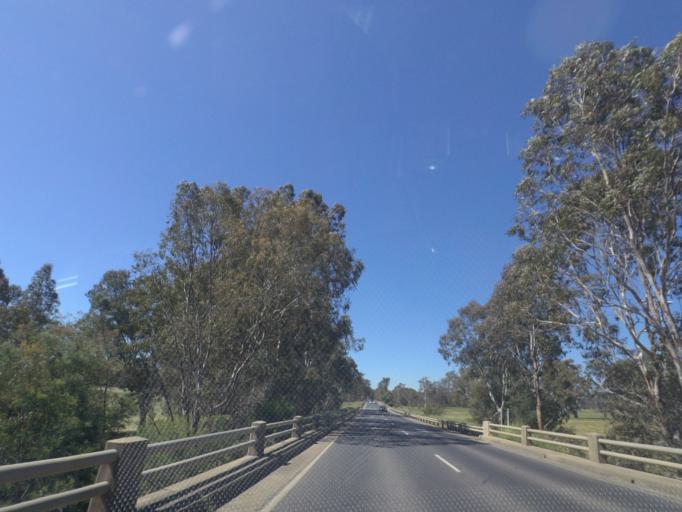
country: AU
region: Victoria
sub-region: Murrindindi
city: Kinglake West
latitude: -37.0276
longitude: 145.1082
